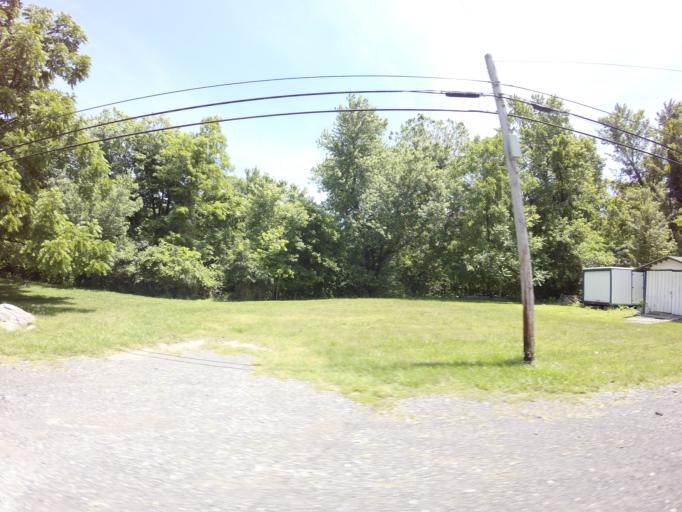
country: US
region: Maryland
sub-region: Frederick County
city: Urbana
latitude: 39.3461
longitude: -77.3756
